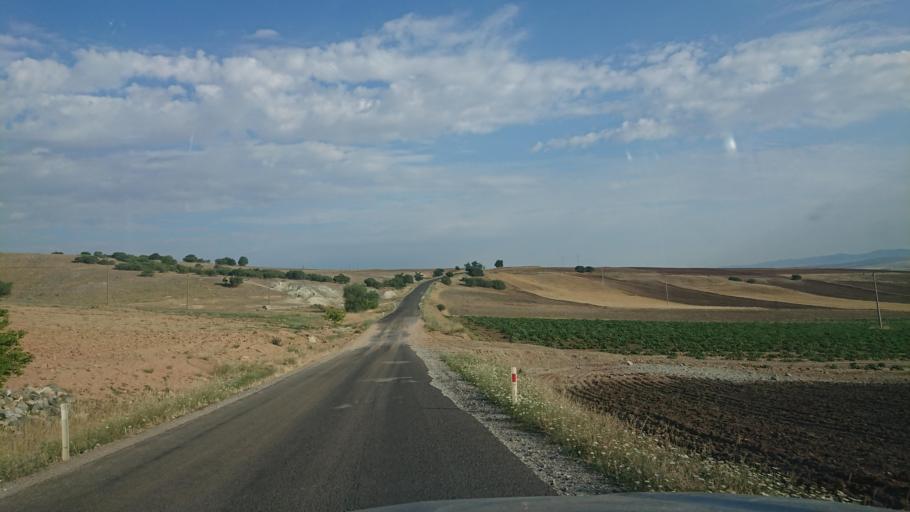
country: TR
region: Aksaray
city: Ortakoy
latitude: 38.8085
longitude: 34.0577
